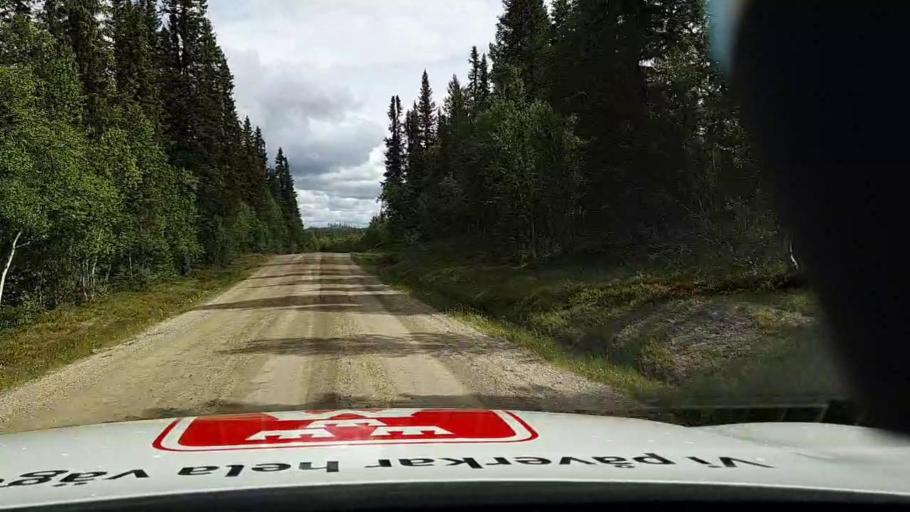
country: SE
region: Jaemtland
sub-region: Are Kommun
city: Jarpen
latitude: 62.5986
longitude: 13.3273
